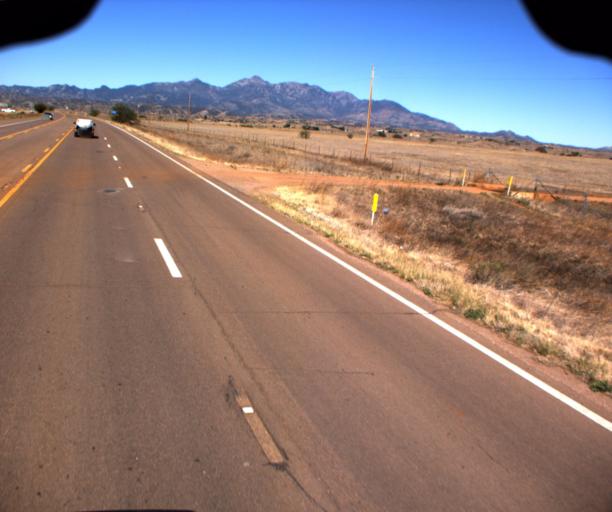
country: US
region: Arizona
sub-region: Pima County
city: Corona de Tucson
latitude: 31.6792
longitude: -110.6572
